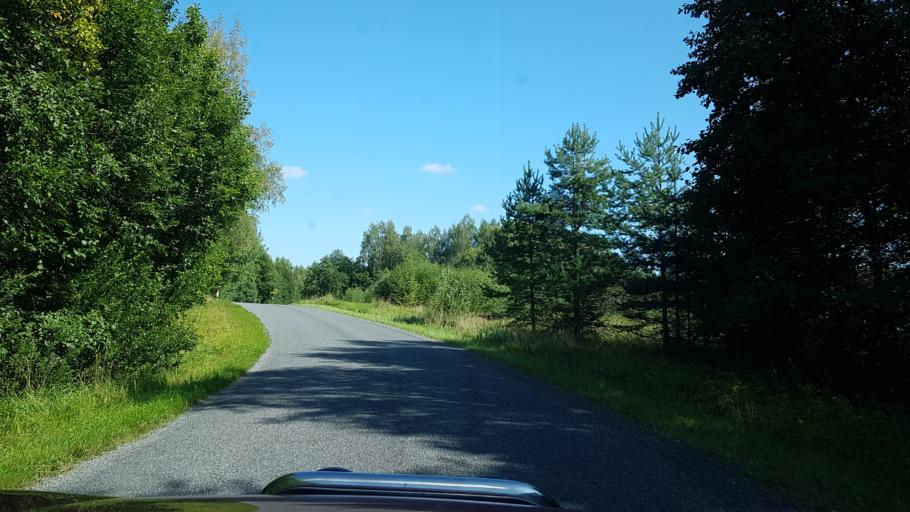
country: EE
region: Vorumaa
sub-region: Voru linn
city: Voru
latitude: 57.7595
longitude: 27.2992
